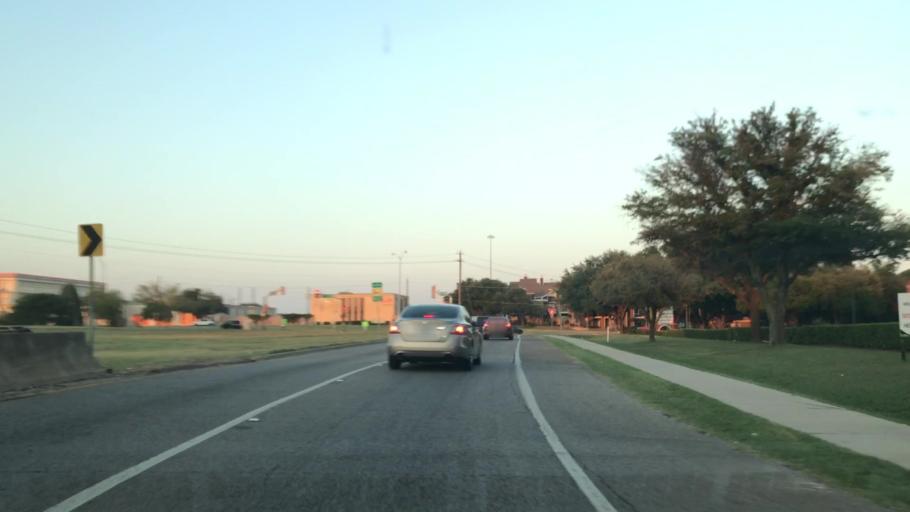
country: US
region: Texas
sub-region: Dallas County
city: Richardson
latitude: 32.8980
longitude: -96.7200
